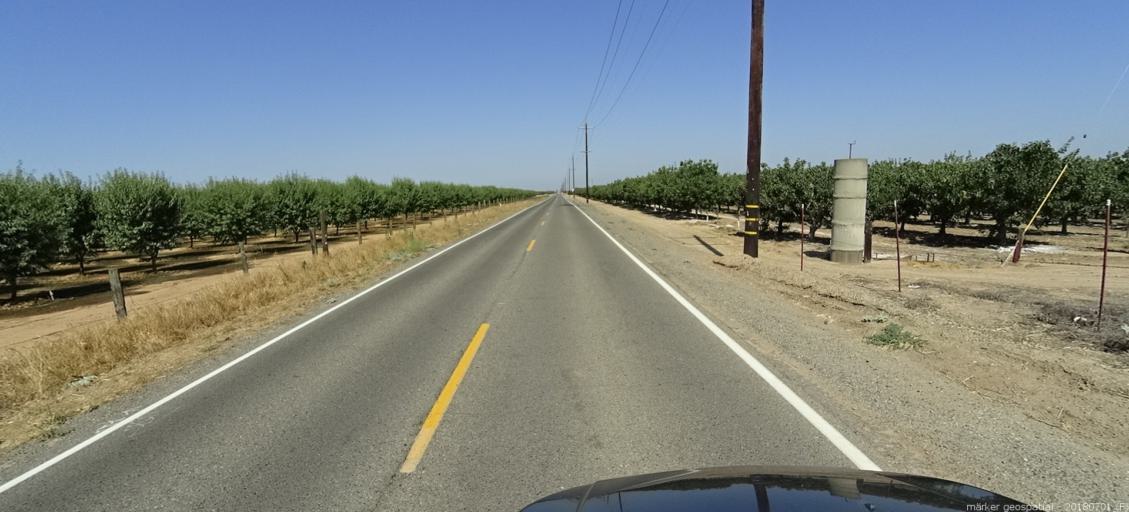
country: US
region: California
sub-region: Madera County
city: Bonadelle Ranchos-Madera Ranchos
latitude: 36.8804
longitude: -119.8440
